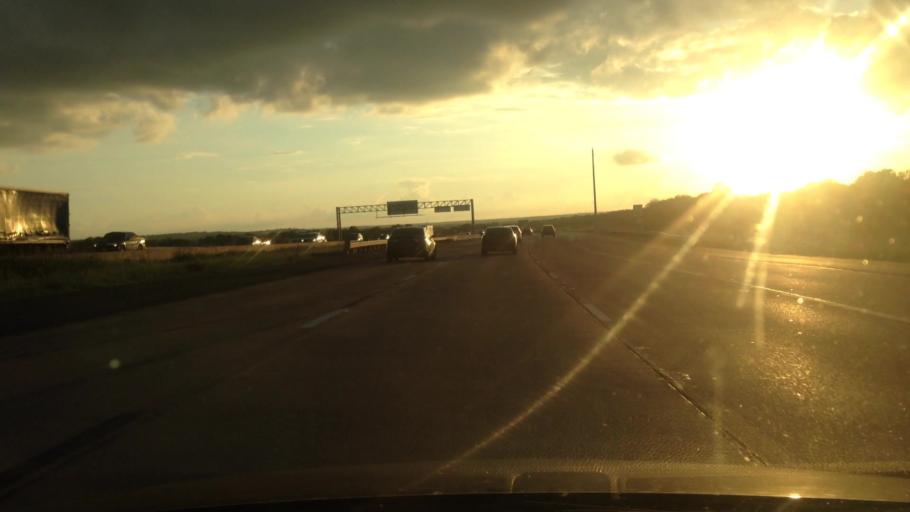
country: US
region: Texas
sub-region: Tarrant County
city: Lake Worth
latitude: 32.7987
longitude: -97.4388
